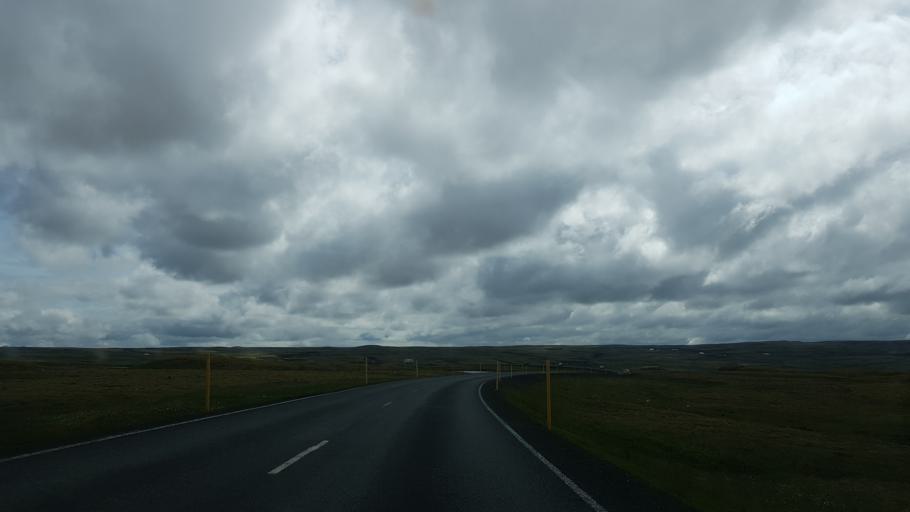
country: IS
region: West
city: Borgarnes
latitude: 64.9509
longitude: -21.0561
